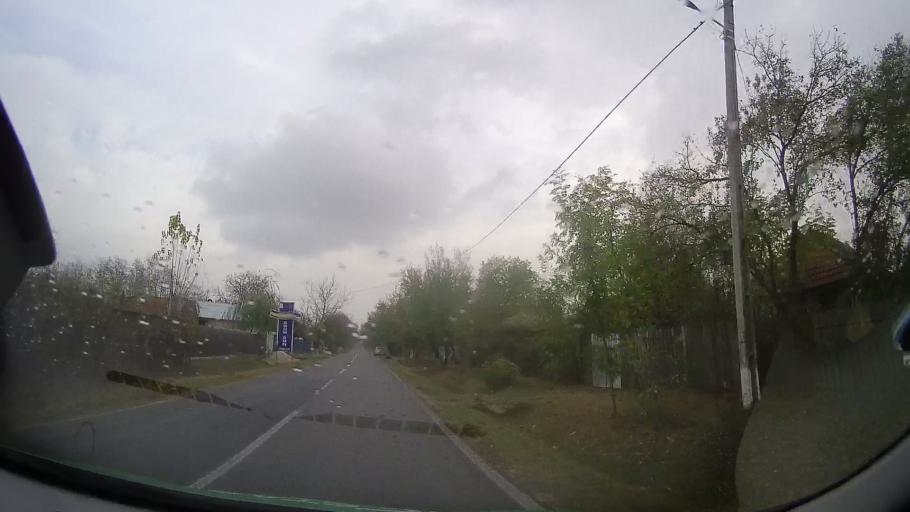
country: RO
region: Prahova
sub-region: Comuna Draganesti
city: Draganesti
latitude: 44.7851
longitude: 26.3178
